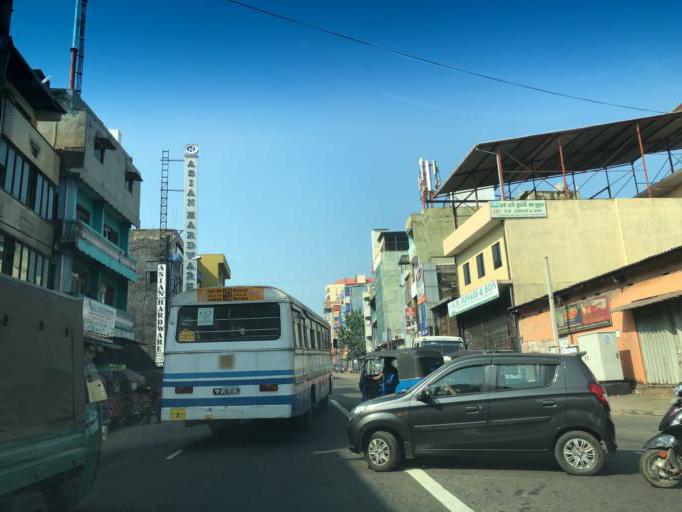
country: LK
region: Western
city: Colombo
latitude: 6.9426
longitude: 79.8623
